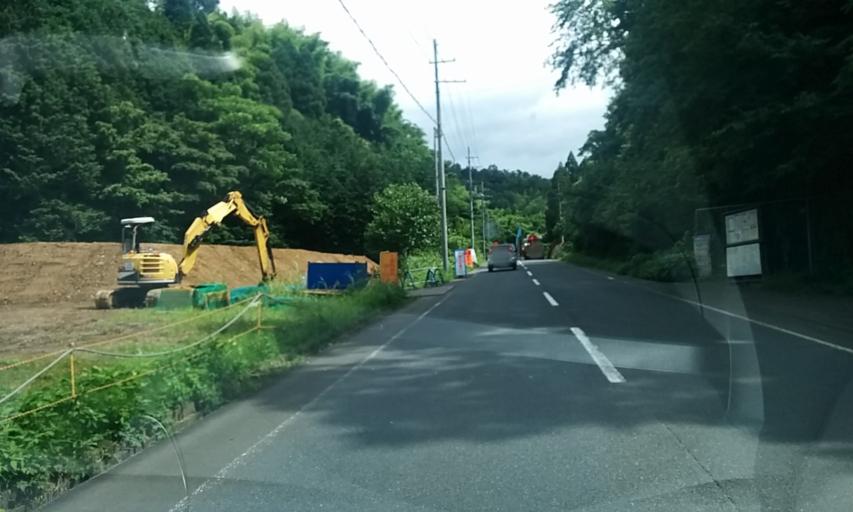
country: JP
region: Kyoto
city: Ayabe
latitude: 35.3510
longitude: 135.2735
